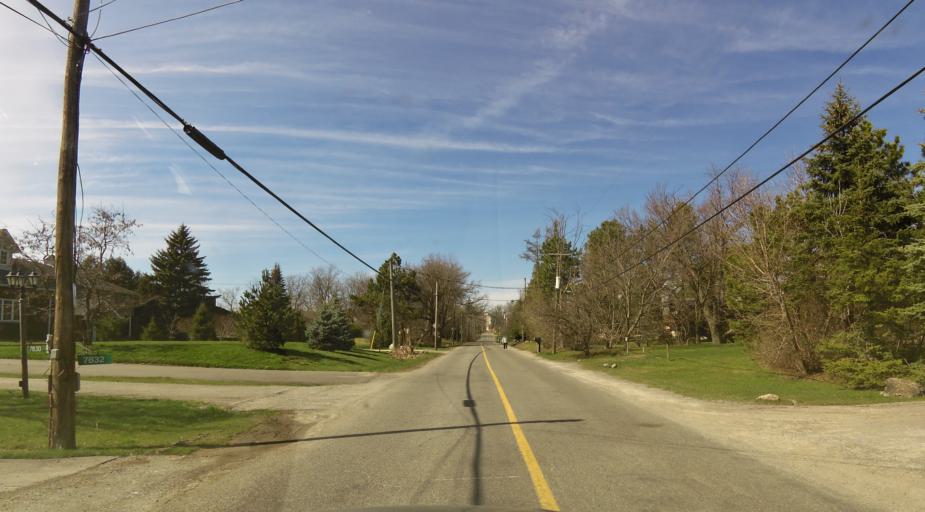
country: CA
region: Ontario
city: Brampton
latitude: 43.6357
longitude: -79.7600
